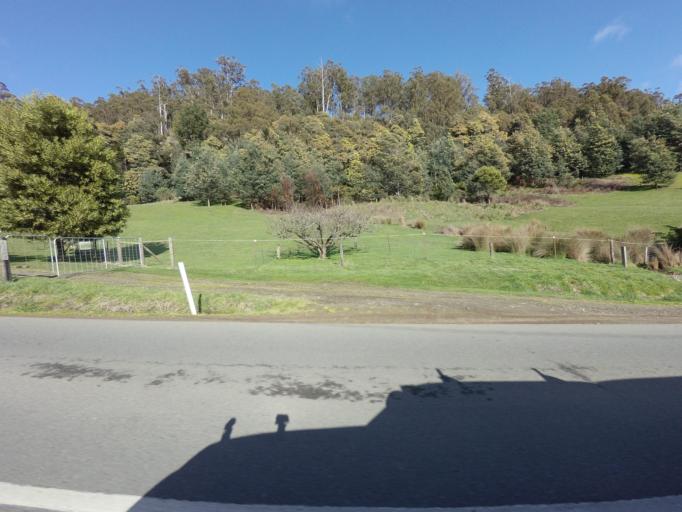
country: AU
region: Tasmania
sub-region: Huon Valley
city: Geeveston
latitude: -43.2472
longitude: 146.9909
